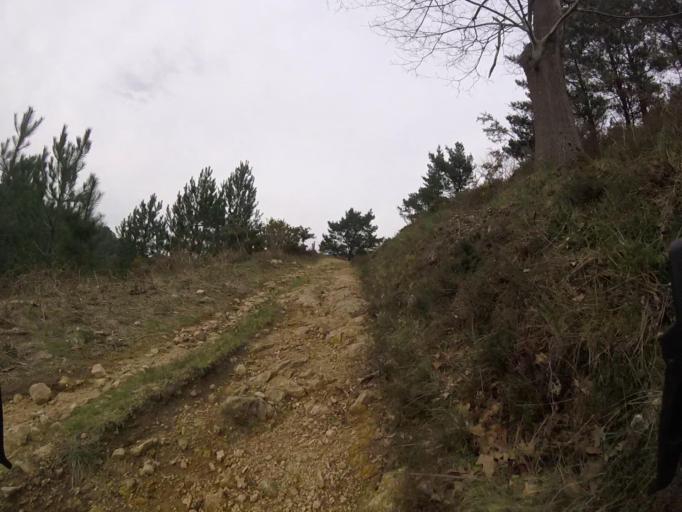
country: ES
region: Navarre
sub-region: Provincia de Navarra
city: Bera
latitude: 43.2917
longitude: -1.7341
